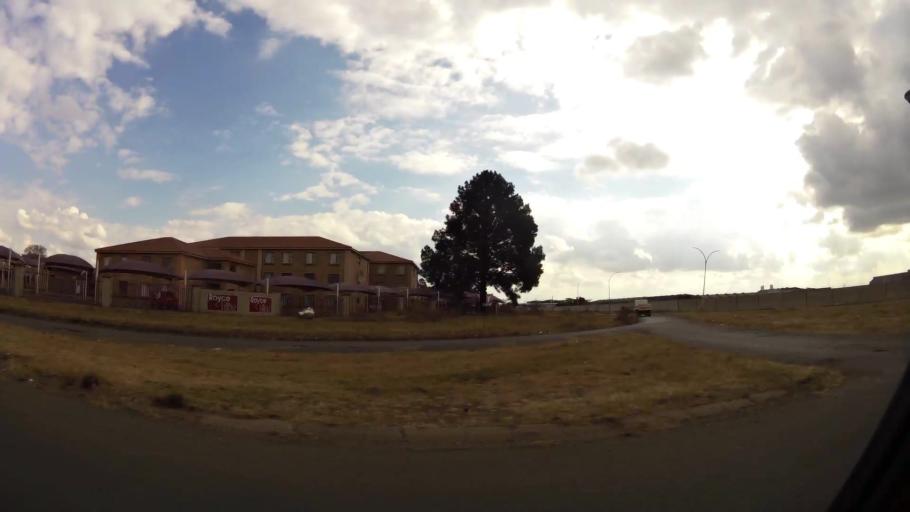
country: ZA
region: Gauteng
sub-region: Sedibeng District Municipality
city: Vanderbijlpark
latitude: -26.6800
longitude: 27.8181
